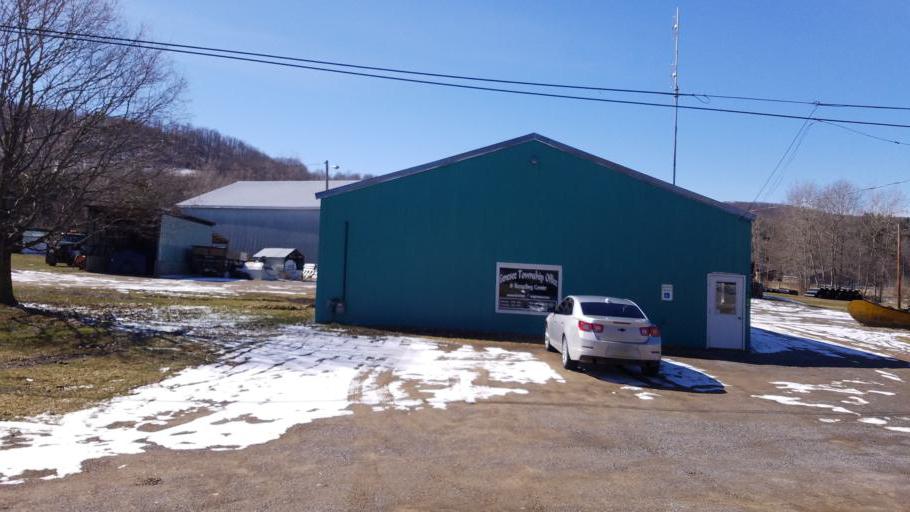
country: US
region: New York
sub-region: Allegany County
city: Wellsville
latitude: 41.9855
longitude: -77.8610
